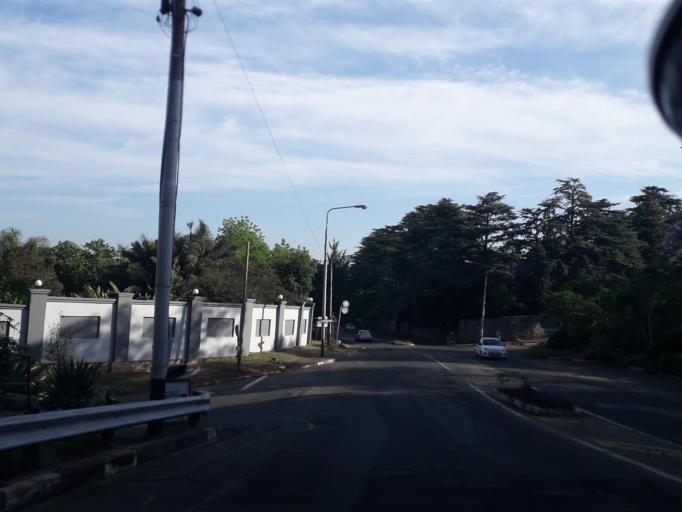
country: ZA
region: Gauteng
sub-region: City of Johannesburg Metropolitan Municipality
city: Johannesburg
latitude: -26.1768
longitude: 28.0197
